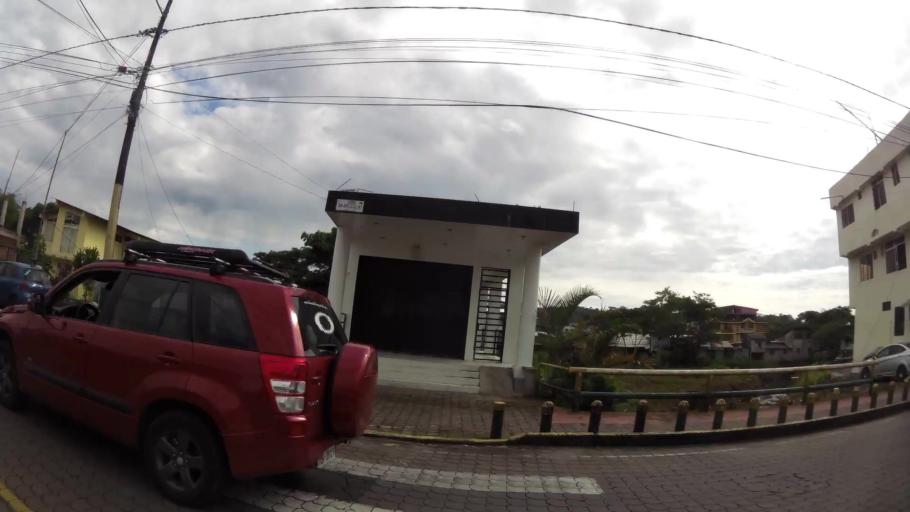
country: EC
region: Pastaza
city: Puyo
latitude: -1.4824
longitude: -77.9993
